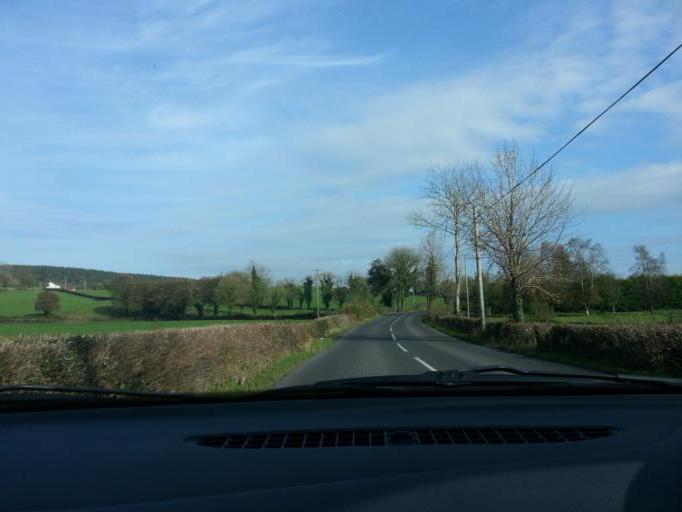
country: IE
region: Ulster
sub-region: County Monaghan
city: Clones
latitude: 54.2257
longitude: -7.3230
